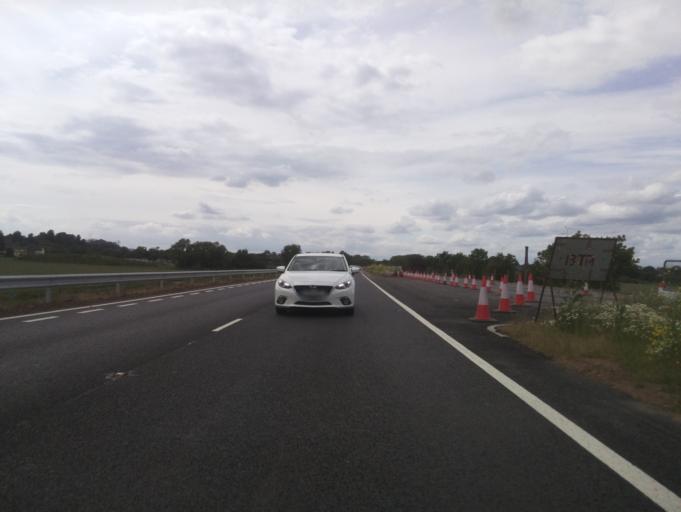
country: GB
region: England
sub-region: Worcestershire
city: Worcester
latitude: 52.1656
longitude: -2.2350
